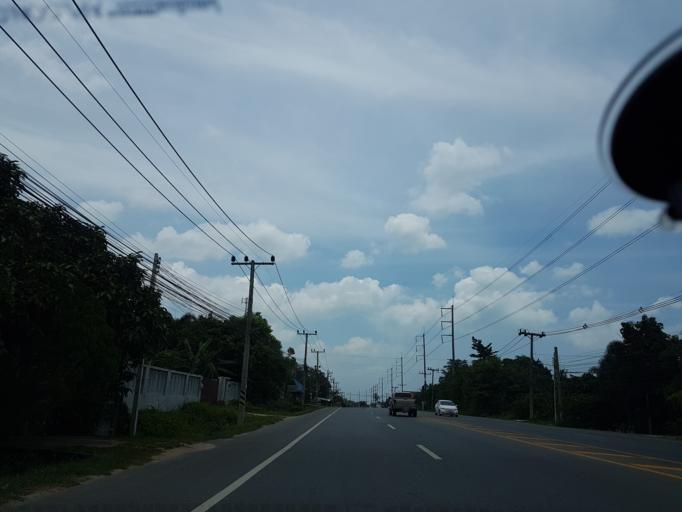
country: TH
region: Songkhla
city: Songkhla
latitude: 7.1205
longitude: 100.6325
